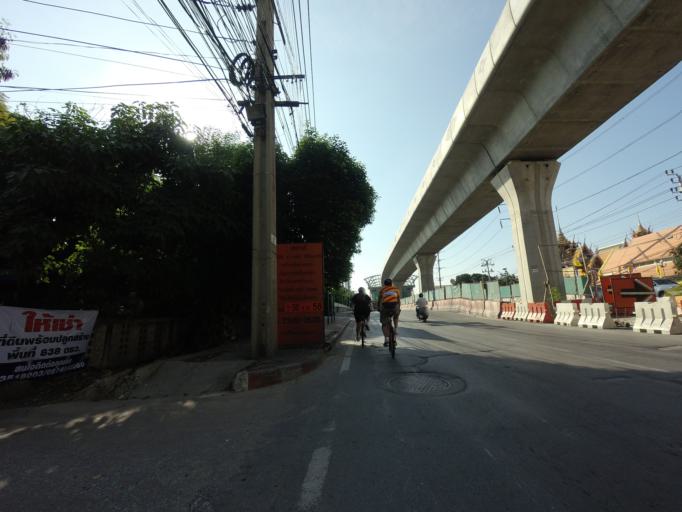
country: TH
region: Samut Prakan
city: Samut Prakan
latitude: 13.6040
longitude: 100.5966
